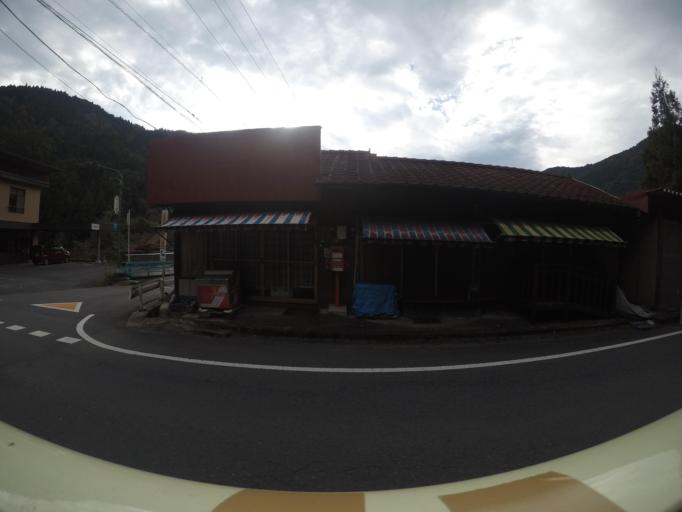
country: JP
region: Gunma
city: Yoshii
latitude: 36.1193
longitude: 138.9395
